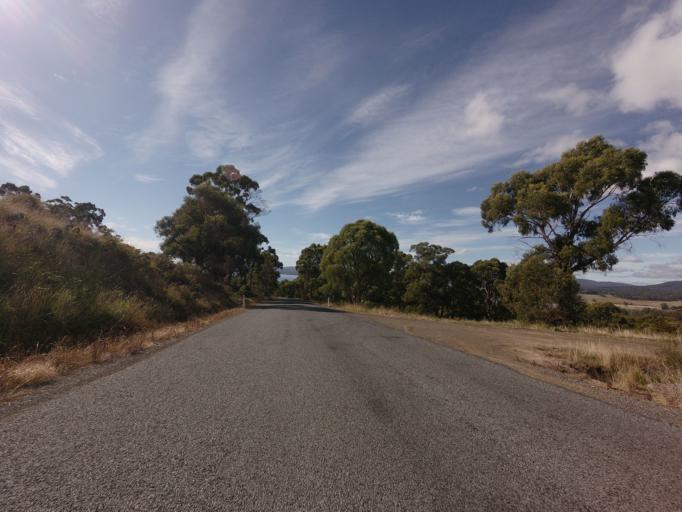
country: AU
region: Tasmania
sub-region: Clarence
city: Sandford
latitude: -43.0385
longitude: 147.7380
